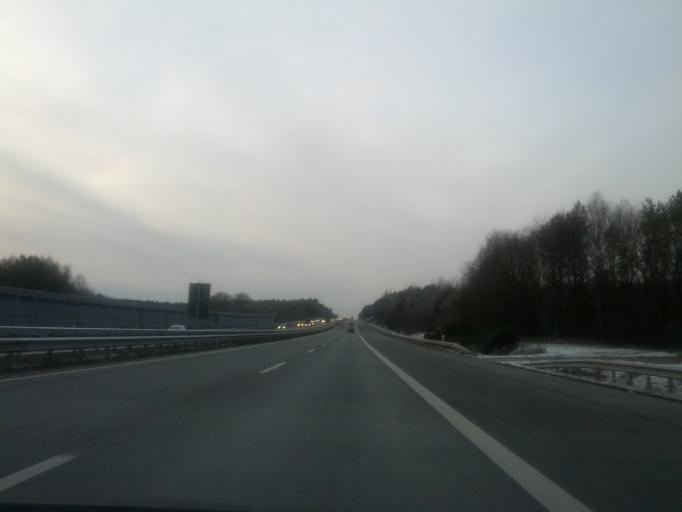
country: DE
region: Lower Saxony
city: Buchholz in der Nordheide
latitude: 53.3730
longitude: 9.8591
